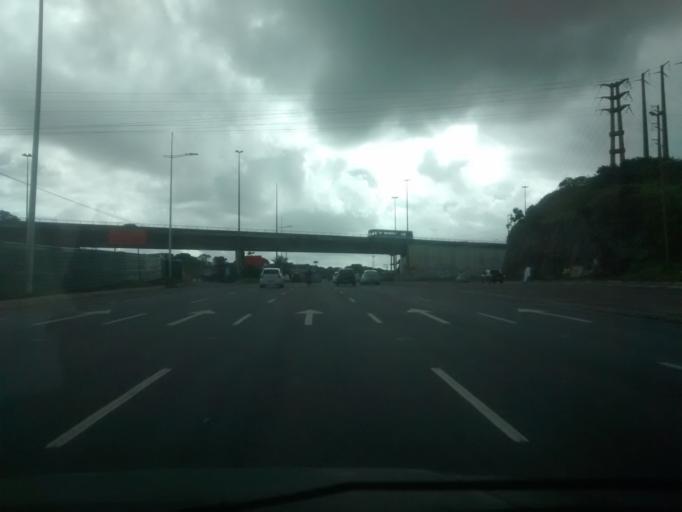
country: BR
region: Bahia
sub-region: Salvador
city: Salvador
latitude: -12.9440
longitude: -38.4199
